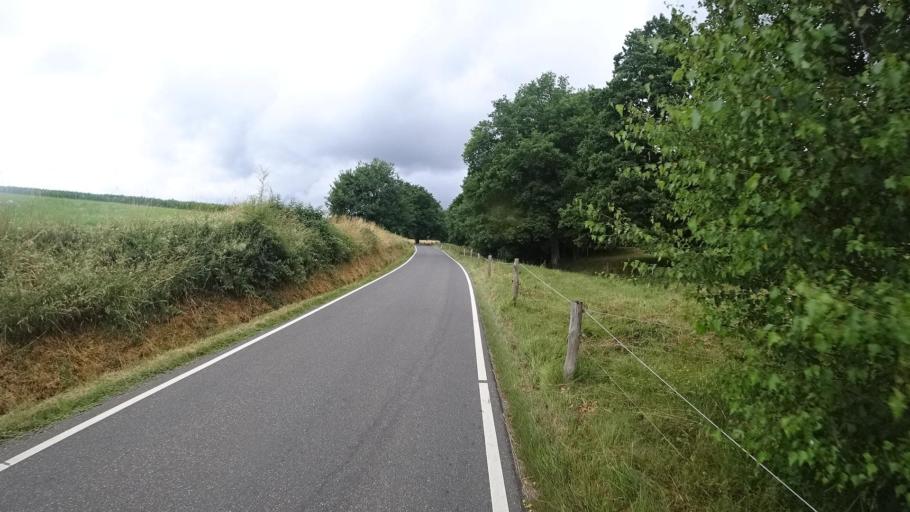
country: DE
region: Rheinland-Pfalz
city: Mehren
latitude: 50.6889
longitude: 7.5060
